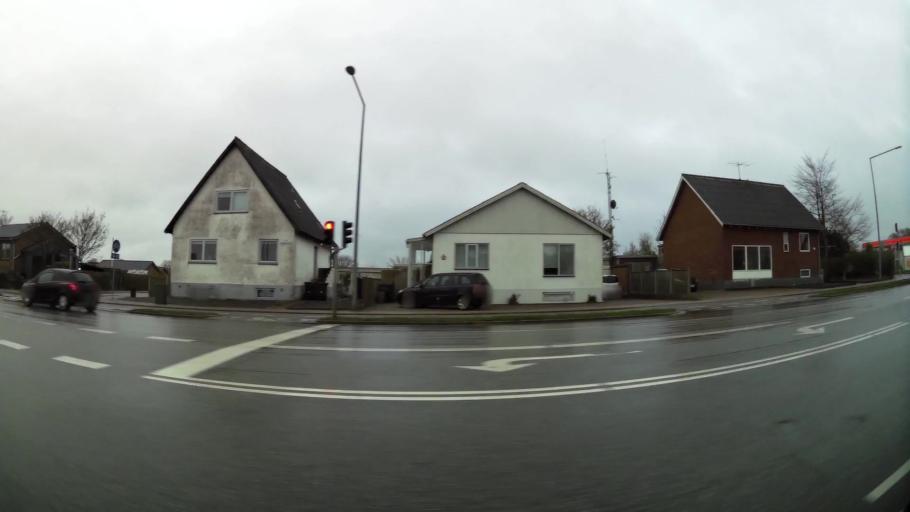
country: DK
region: Central Jutland
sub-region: Herning Kommune
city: Herning
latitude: 56.1378
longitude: 8.9472
